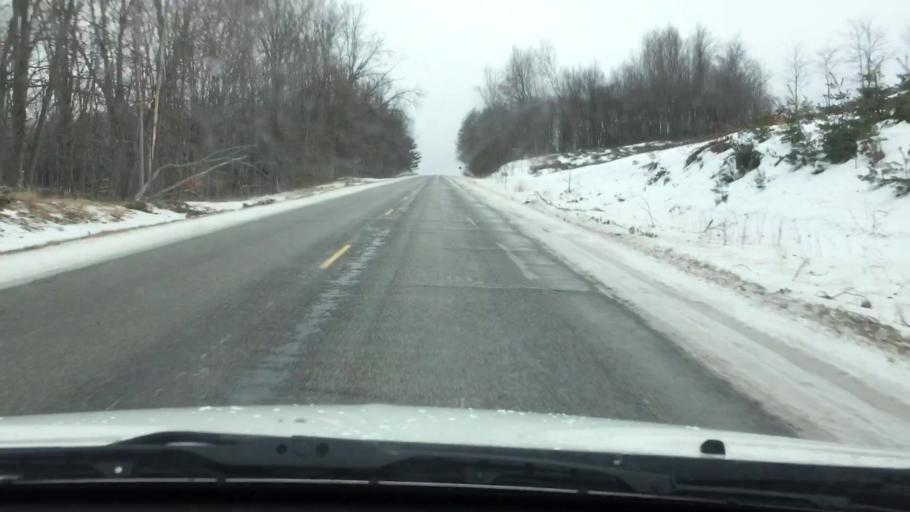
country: US
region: Michigan
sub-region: Wexford County
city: Cadillac
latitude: 44.1698
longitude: -85.4054
